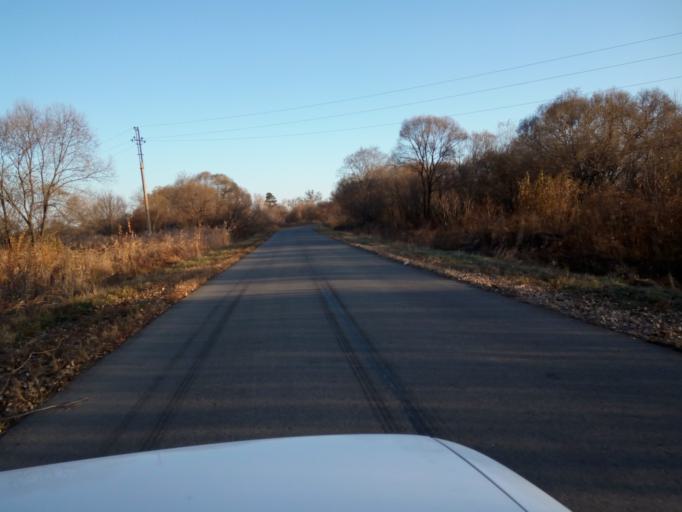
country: RU
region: Primorskiy
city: Lazo
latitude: 45.8593
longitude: 133.6396
